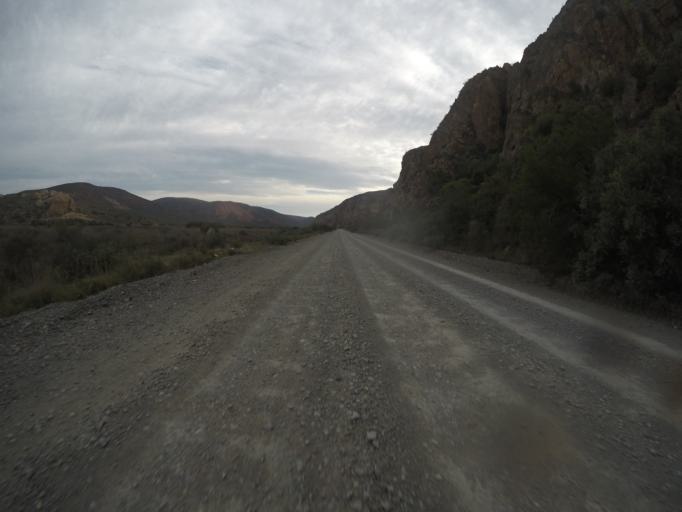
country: ZA
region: Eastern Cape
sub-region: Cacadu District Municipality
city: Willowmore
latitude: -33.5199
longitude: 23.6684
